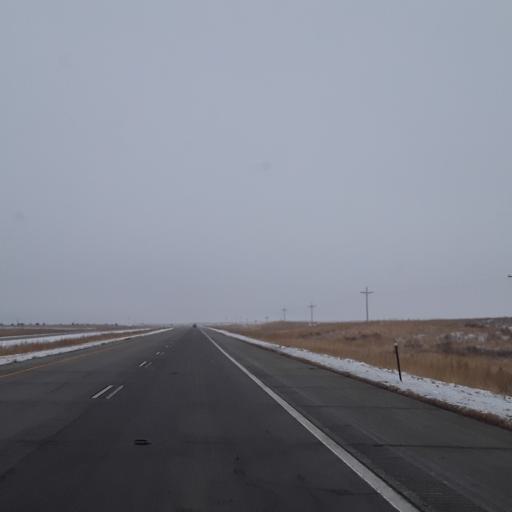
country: US
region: Colorado
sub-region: Logan County
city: Sterling
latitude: 40.5245
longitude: -103.2380
